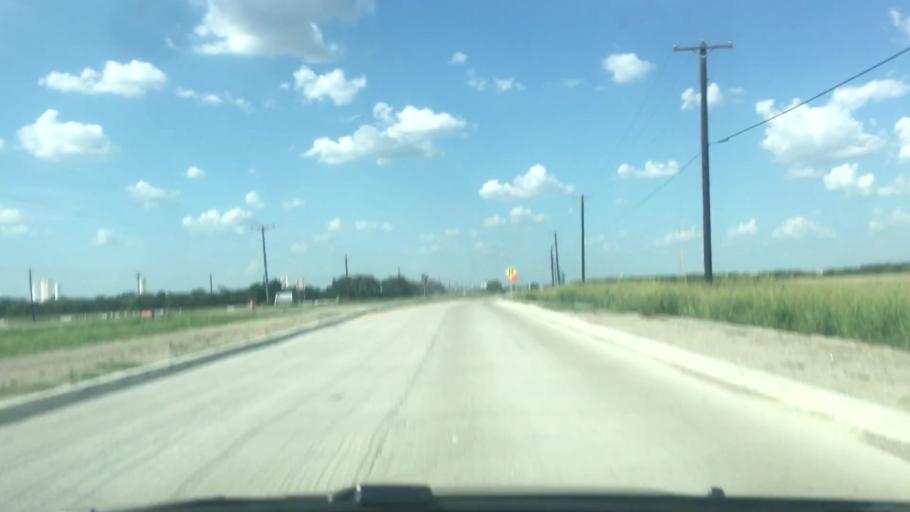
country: US
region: Texas
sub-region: Collin County
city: Prosper
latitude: 33.2215
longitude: -96.8195
